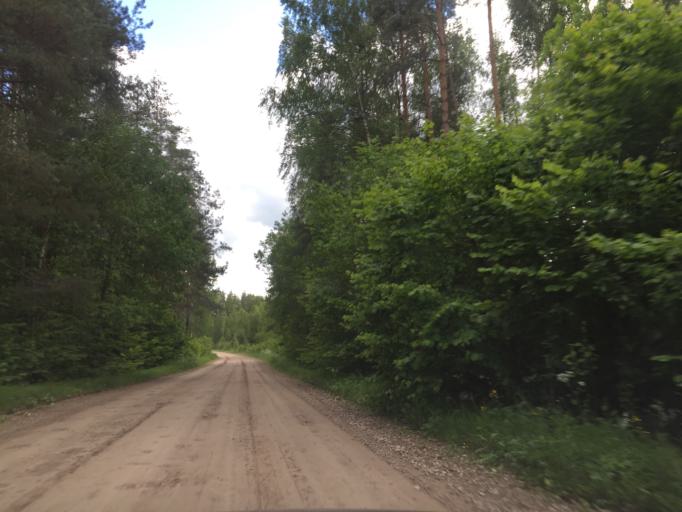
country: LV
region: Vecumnieki
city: Vecumnieki
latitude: 56.4953
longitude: 24.4081
